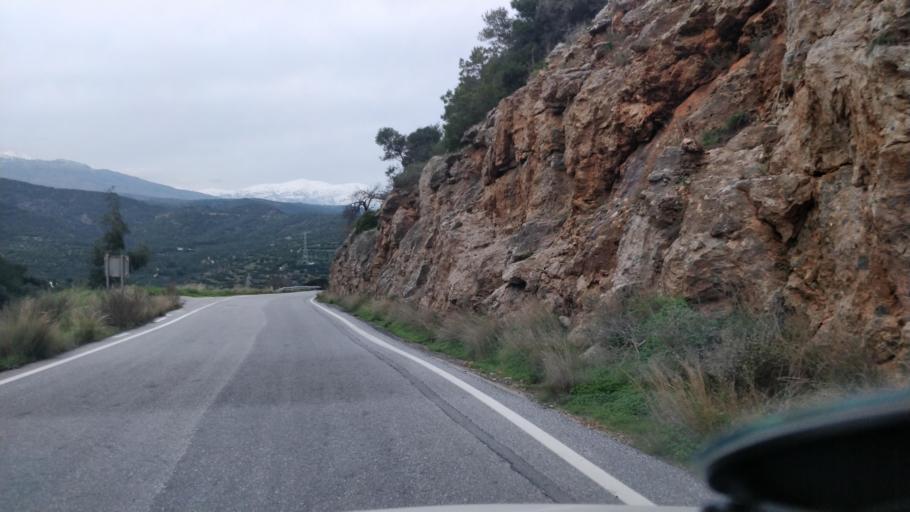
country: GR
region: Crete
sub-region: Nomos Lasithiou
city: Agios Nikolaos
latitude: 35.1111
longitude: 25.7214
